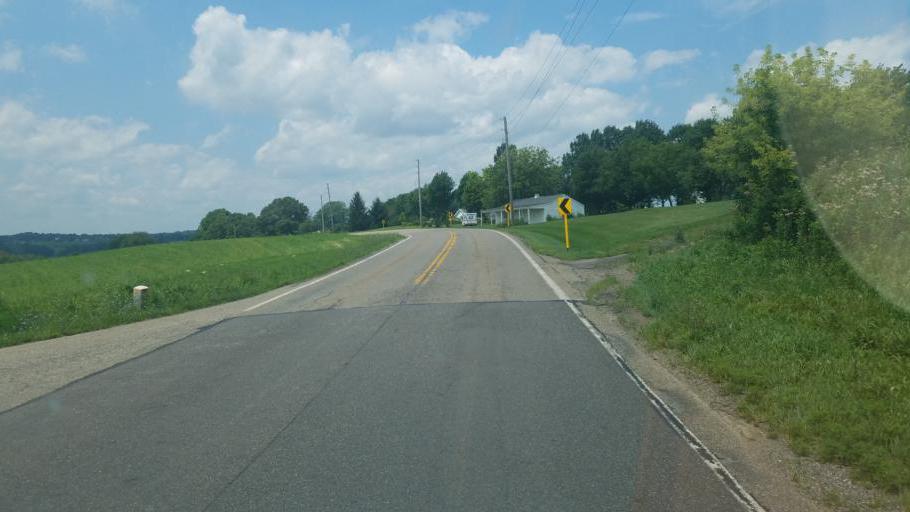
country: US
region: Ohio
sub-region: Stark County
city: Minerva
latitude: 40.7948
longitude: -81.0553
